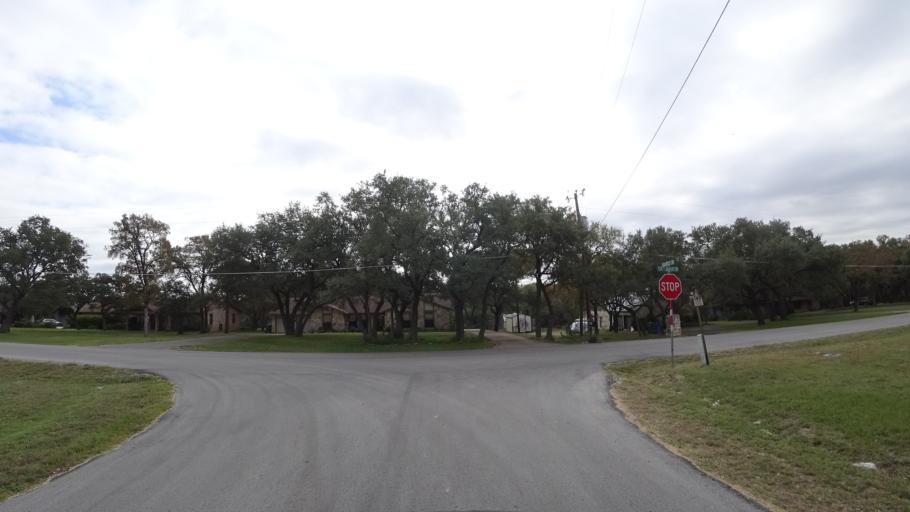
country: US
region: Texas
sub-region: Travis County
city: Shady Hollow
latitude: 30.1447
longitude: -97.8835
